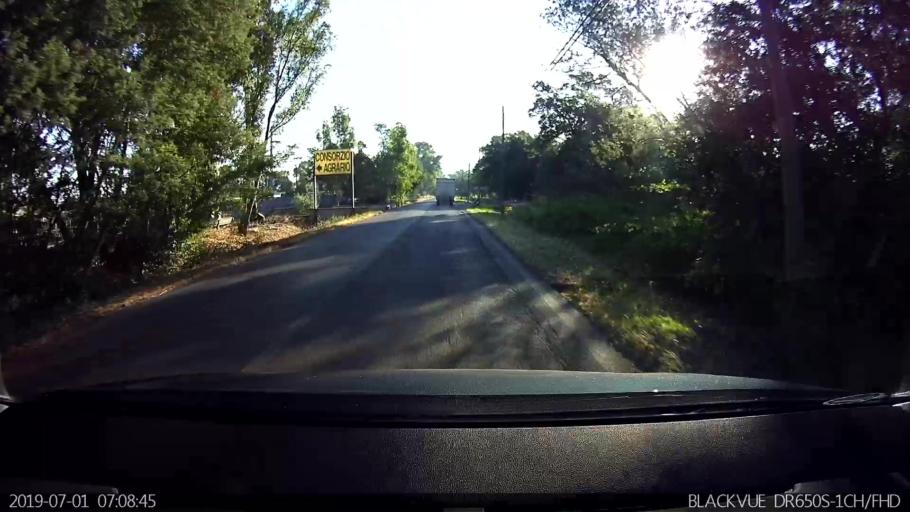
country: IT
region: Latium
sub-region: Provincia di Latina
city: Borgo Hermada
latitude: 41.3000
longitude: 13.1538
